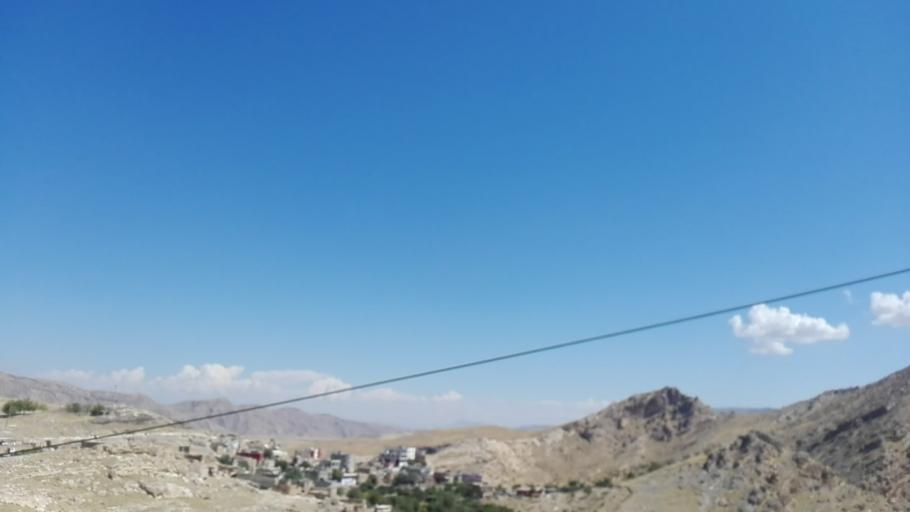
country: TR
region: Batman
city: Hasankeyf
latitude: 37.7030
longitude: 41.4621
